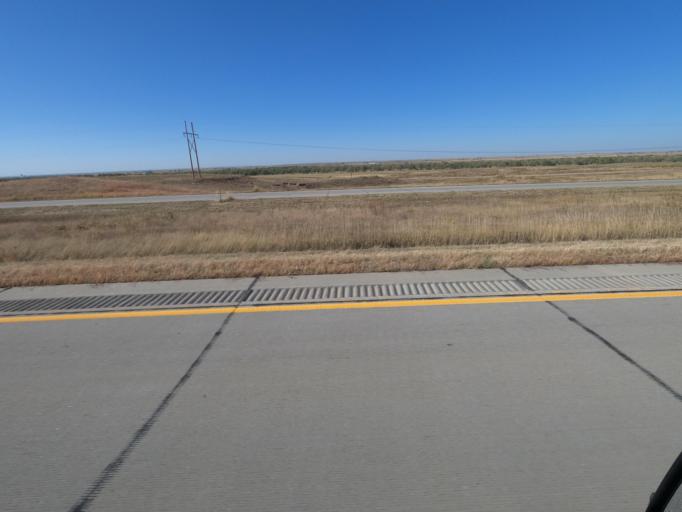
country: US
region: Colorado
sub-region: Sedgwick County
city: Julesburg
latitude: 40.9409
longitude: -102.2955
